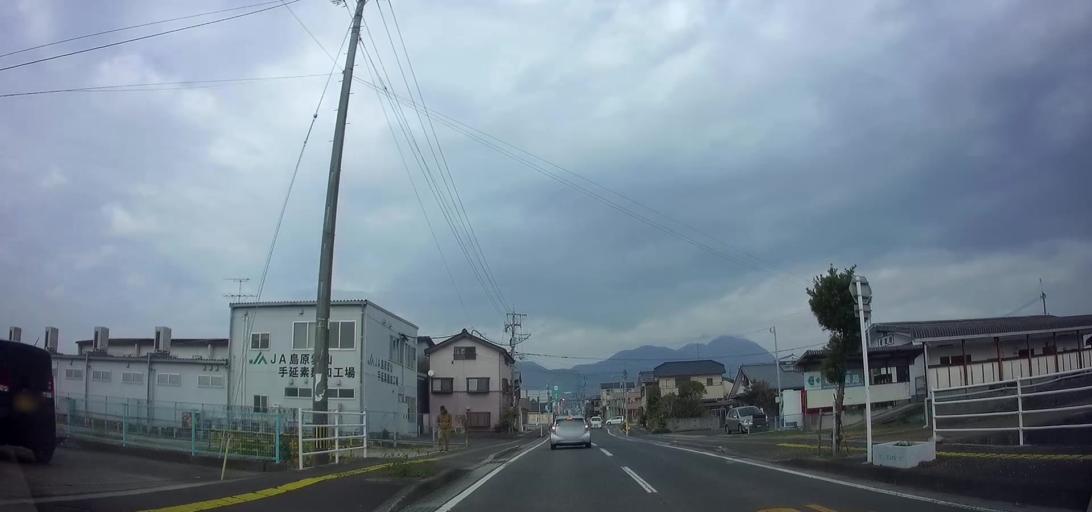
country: JP
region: Nagasaki
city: Shimabara
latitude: 32.6635
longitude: 130.3047
